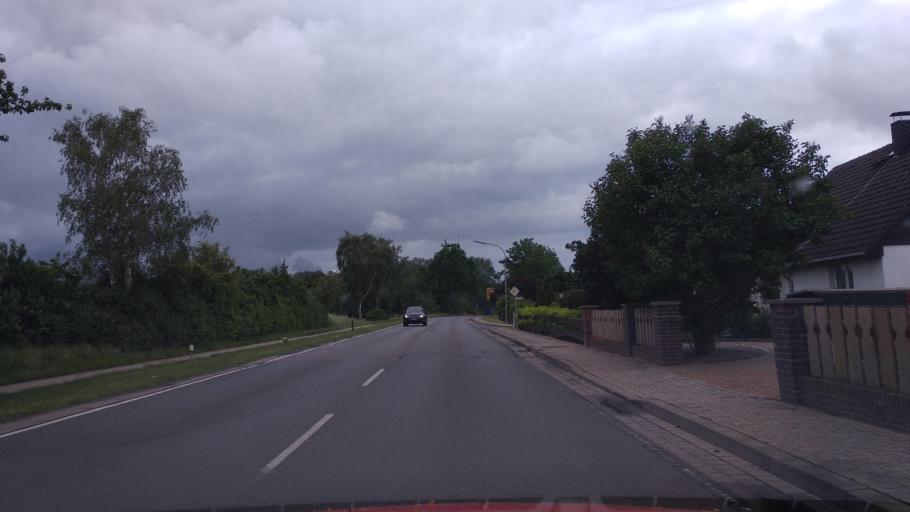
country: DE
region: Lower Saxony
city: Hagenburg
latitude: 52.4404
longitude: 9.3503
